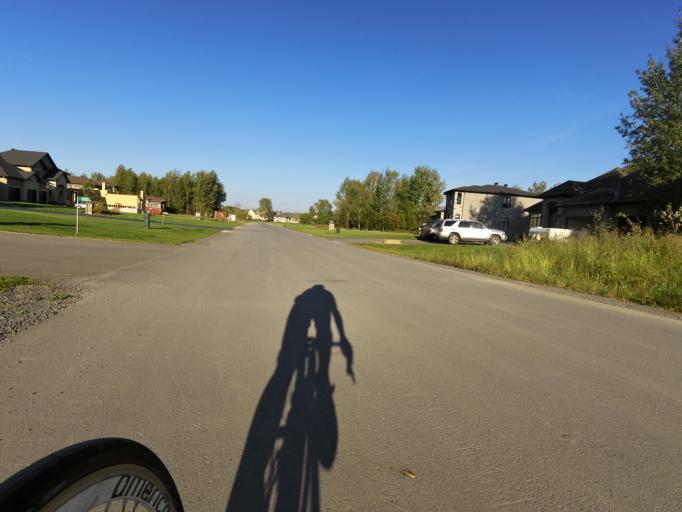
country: CA
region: Ontario
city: Bells Corners
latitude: 45.2128
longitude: -75.7057
